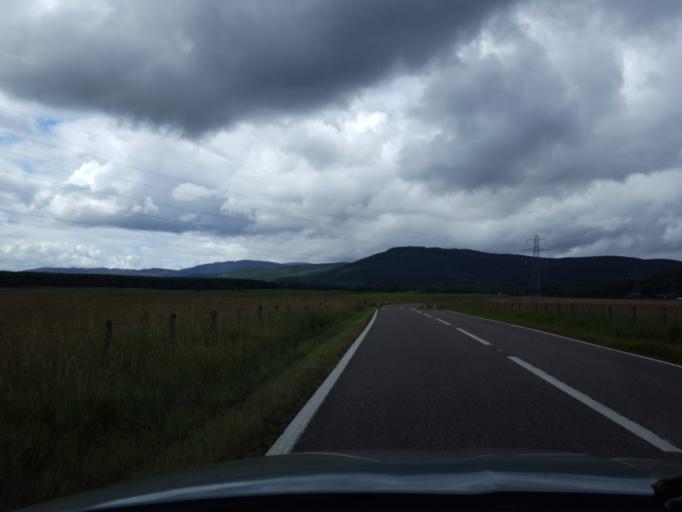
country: GB
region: Scotland
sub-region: Highland
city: Aviemore
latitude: 57.2566
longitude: -3.7614
